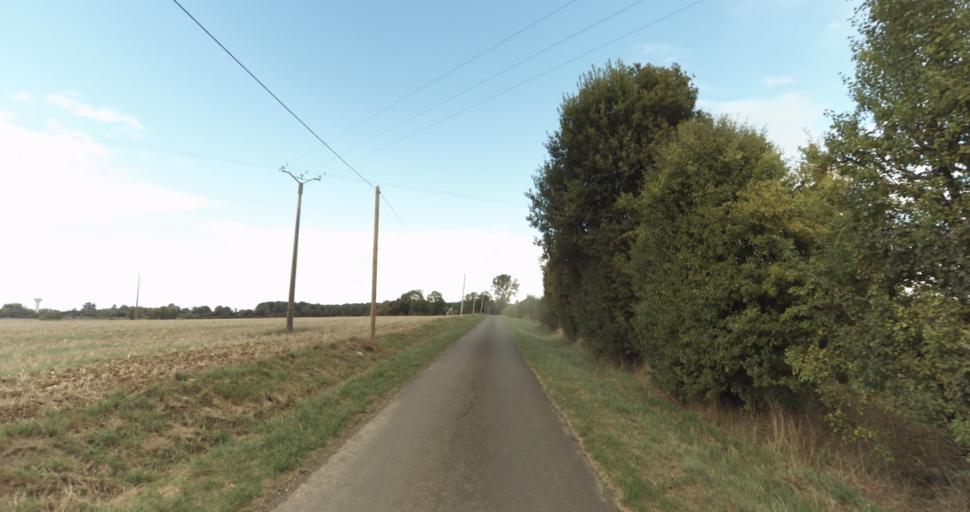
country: FR
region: Lower Normandy
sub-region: Departement de l'Orne
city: Sainte-Gauburge-Sainte-Colombe
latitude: 48.7444
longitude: 0.4073
